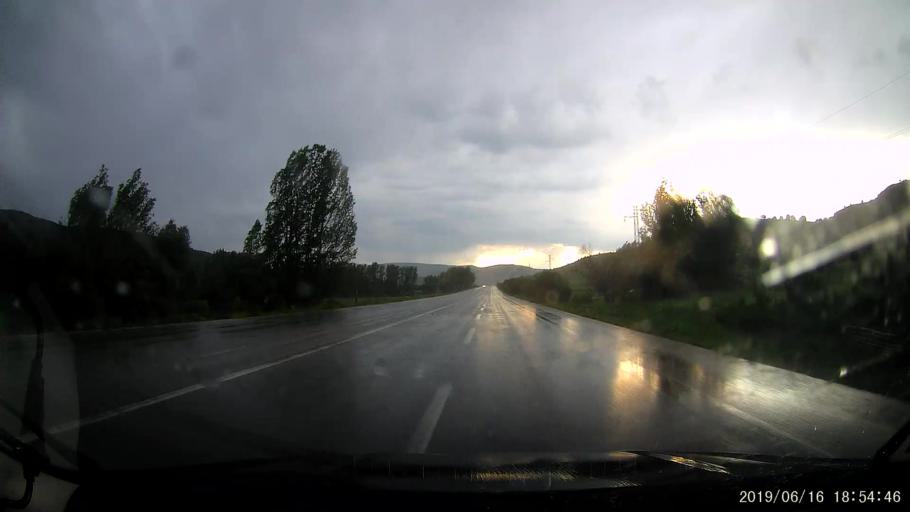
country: TR
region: Erzincan
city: Catalcam
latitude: 39.8980
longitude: 38.8452
